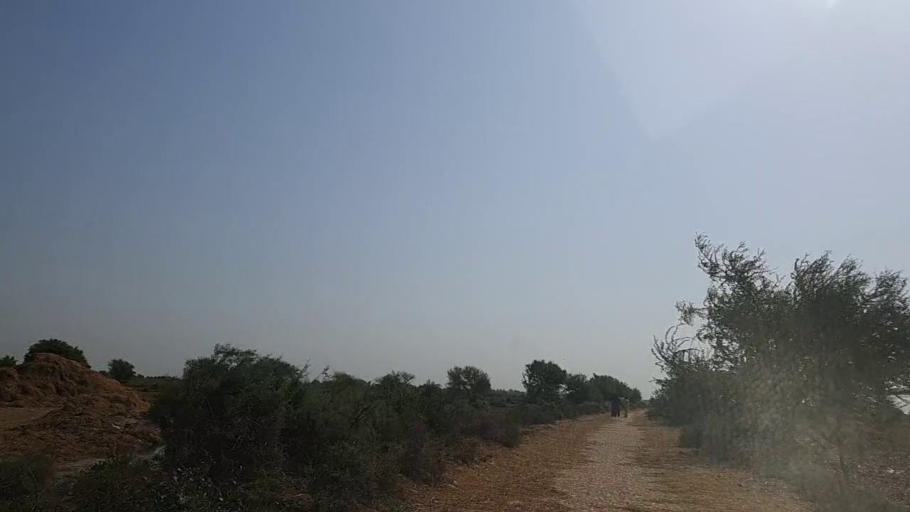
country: PK
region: Sindh
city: Daro Mehar
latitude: 24.7182
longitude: 68.1163
